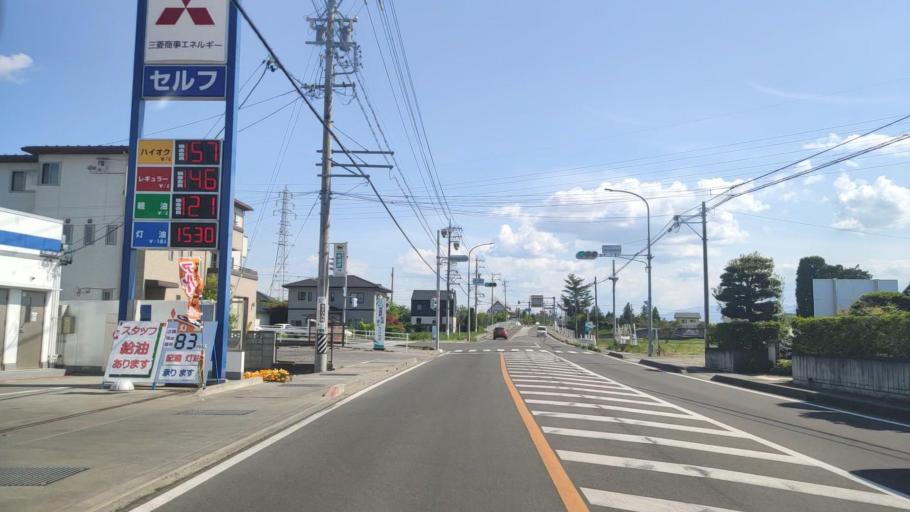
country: JP
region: Nagano
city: Toyoshina
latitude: 36.2861
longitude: 137.9080
